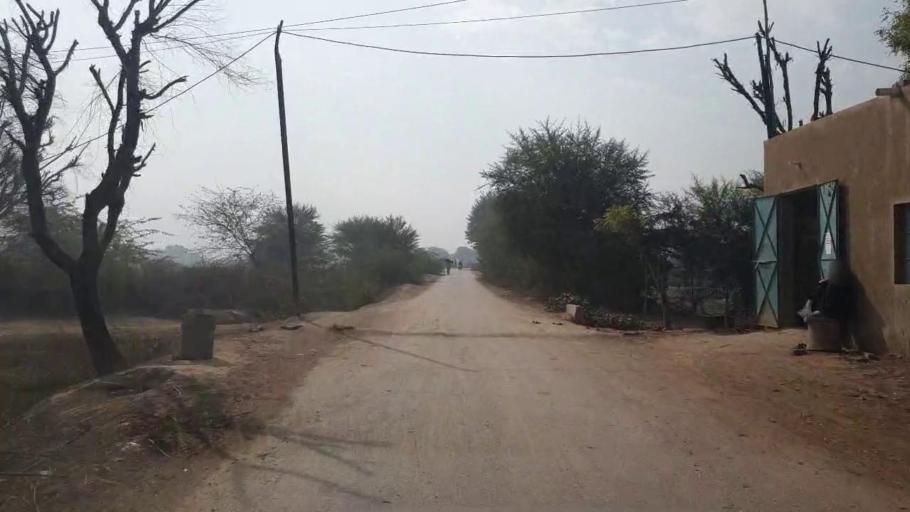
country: PK
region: Sindh
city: Hala
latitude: 25.7523
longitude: 68.4454
